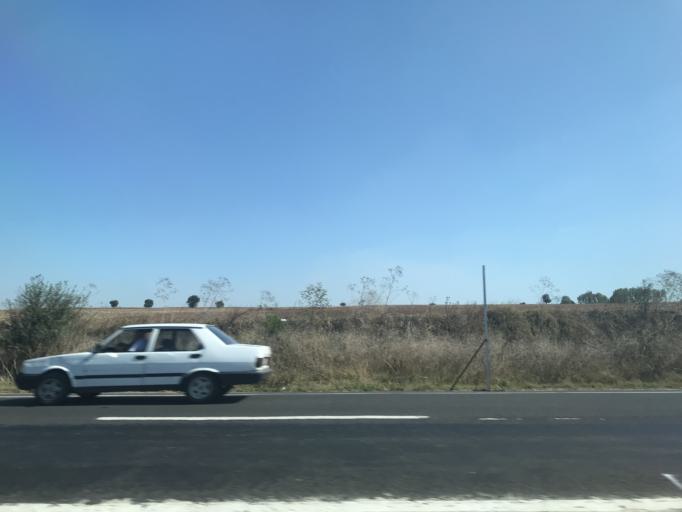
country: TR
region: Tekirdag
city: Muratli
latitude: 41.1338
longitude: 27.4894
